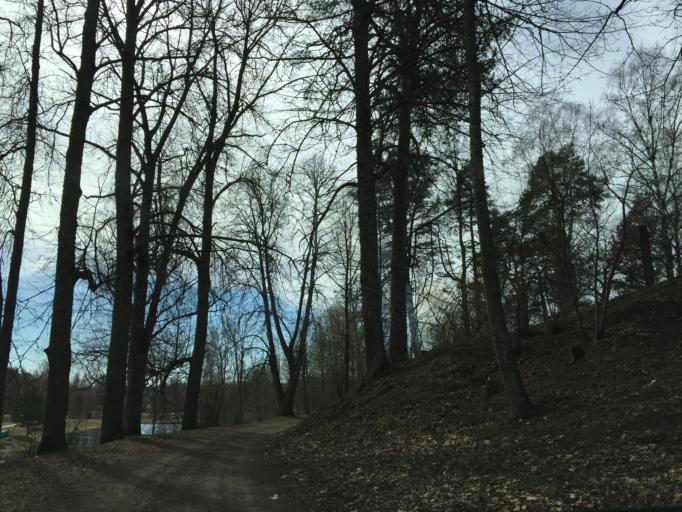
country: LV
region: Strenci
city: Seda
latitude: 57.8101
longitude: 25.8254
